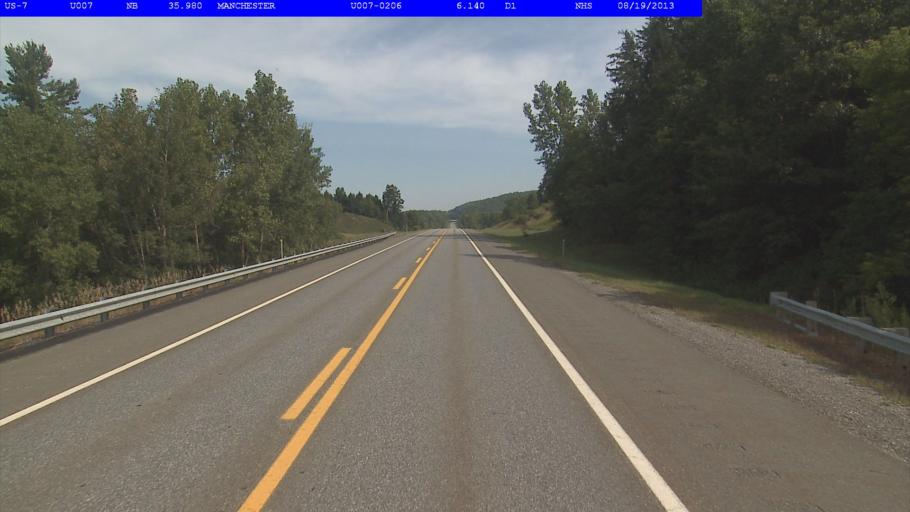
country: US
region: Vermont
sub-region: Bennington County
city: Manchester Center
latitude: 43.1909
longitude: -73.0142
